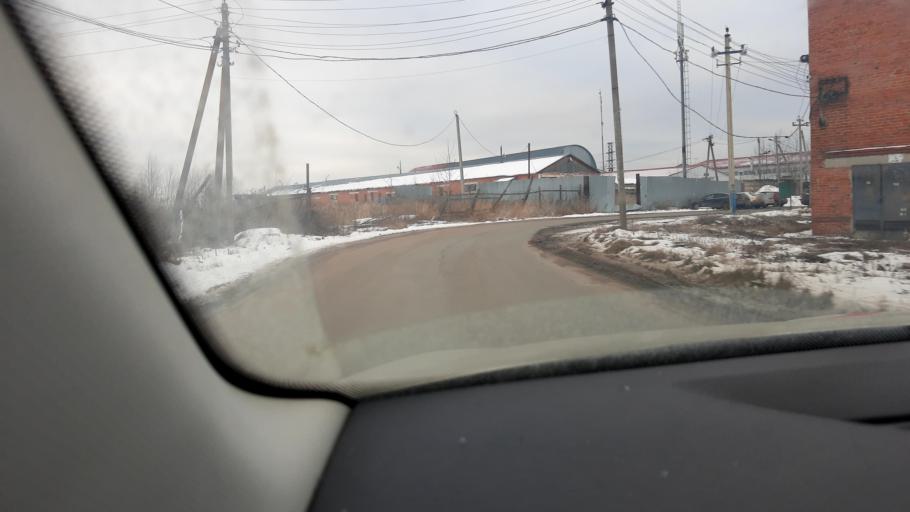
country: RU
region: Moskovskaya
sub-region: Leninskiy Rayon
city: Molokovo
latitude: 55.4891
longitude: 37.8577
